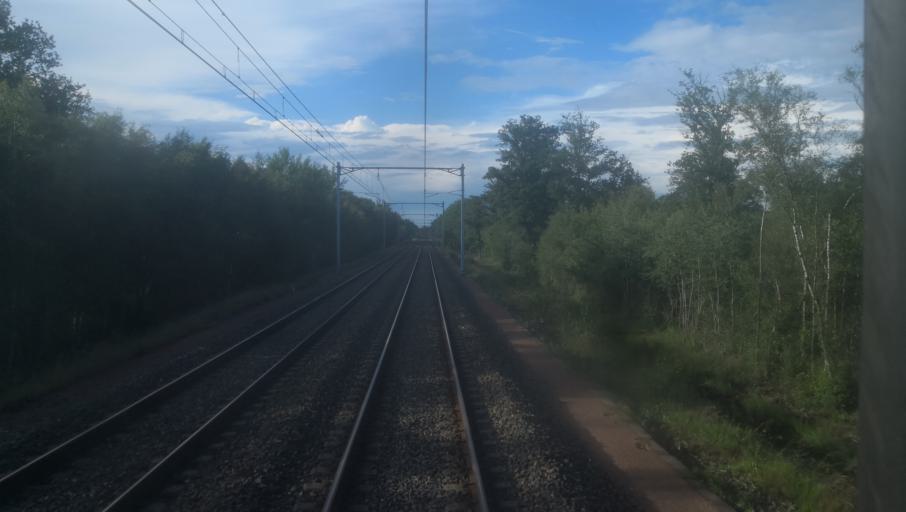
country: FR
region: Centre
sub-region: Departement du Loir-et-Cher
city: Salbris
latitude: 47.3894
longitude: 2.0511
